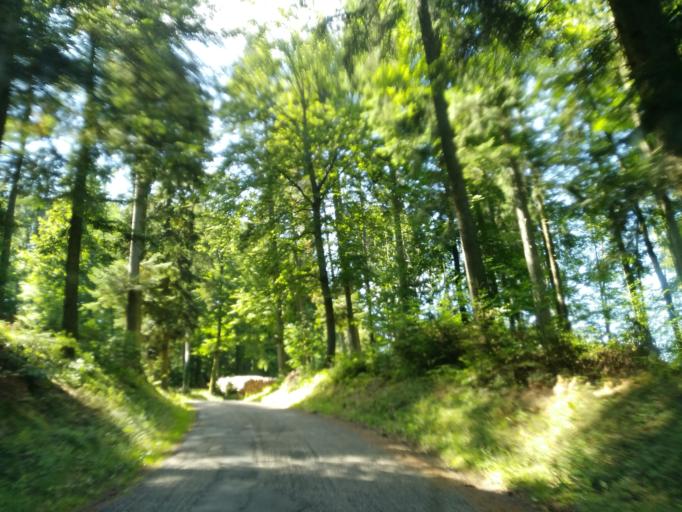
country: DE
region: Baden-Wuerttemberg
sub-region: Karlsruhe Region
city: Limbach
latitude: 49.4584
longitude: 9.2237
